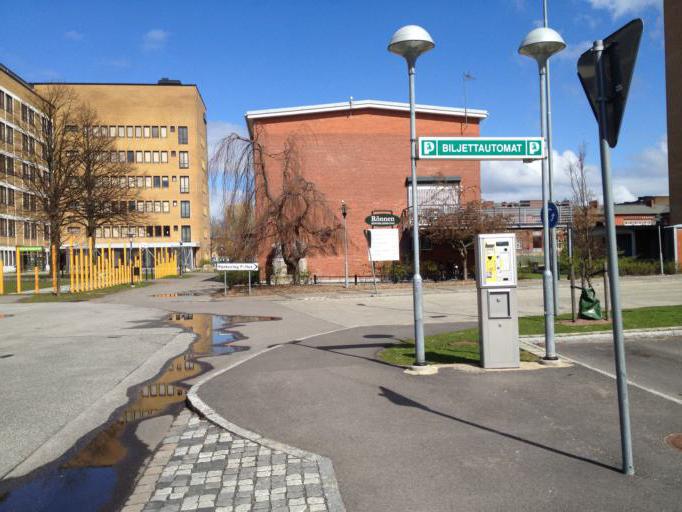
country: SE
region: Skane
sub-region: Malmo
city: Malmoe
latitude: 55.6013
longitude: 13.0285
